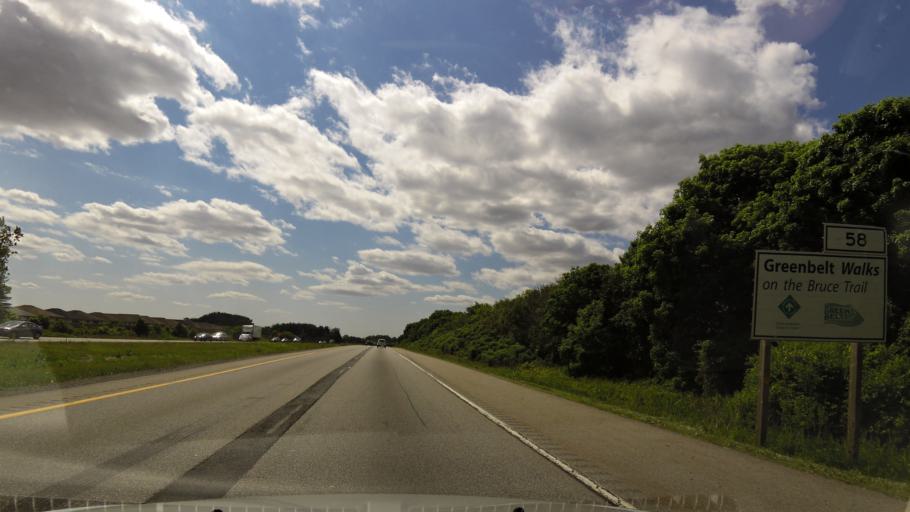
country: CA
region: Ontario
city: Ancaster
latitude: 43.2046
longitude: -79.9913
